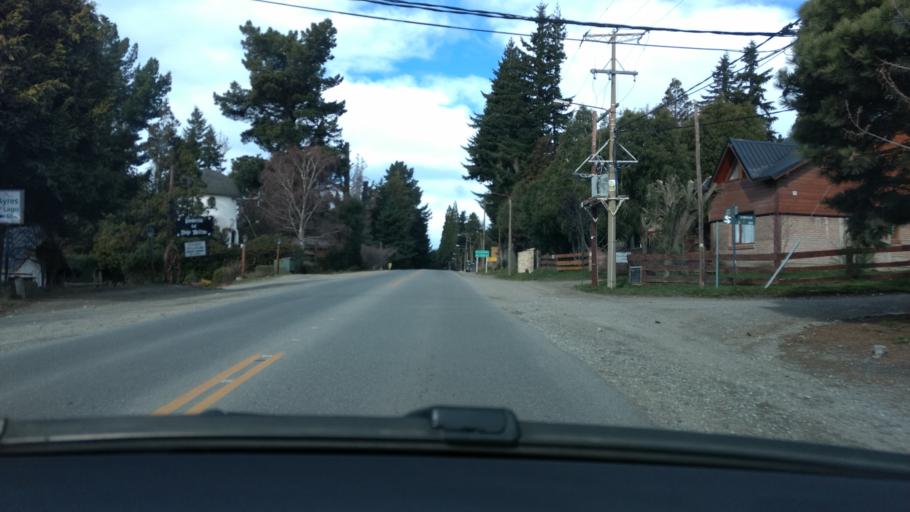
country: AR
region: Rio Negro
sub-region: Departamento de Bariloche
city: San Carlos de Bariloche
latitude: -41.1203
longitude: -71.3793
